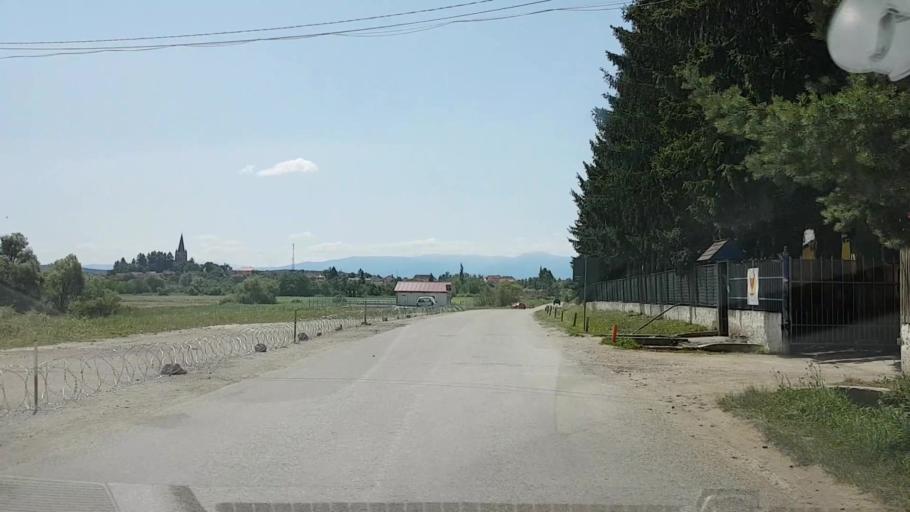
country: RO
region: Brasov
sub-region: Comuna Cincu
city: Cincu
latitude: 45.9242
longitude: 24.7974
